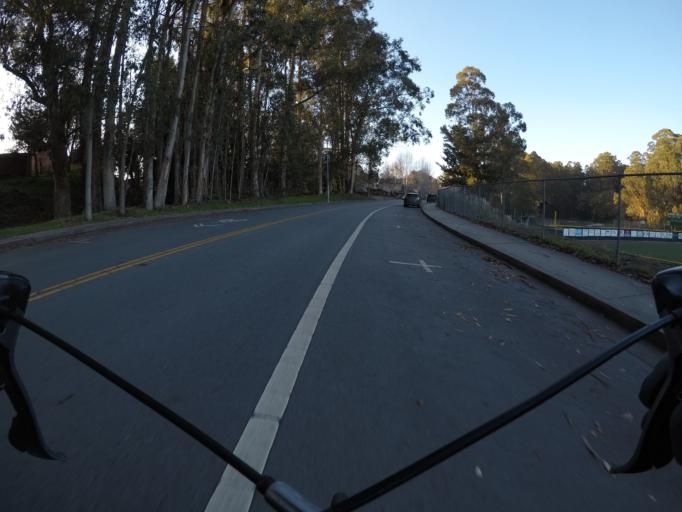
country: US
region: California
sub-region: Santa Cruz County
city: Live Oak
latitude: 36.9842
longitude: -121.9956
